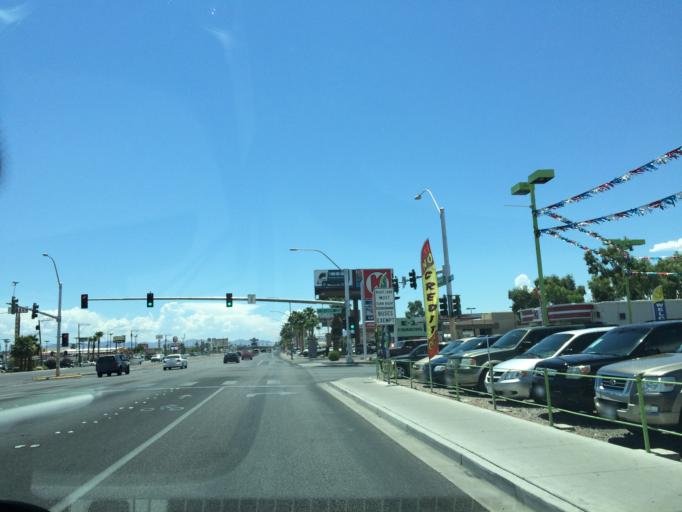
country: US
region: Nevada
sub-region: Clark County
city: Winchester
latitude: 36.1489
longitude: -115.1053
